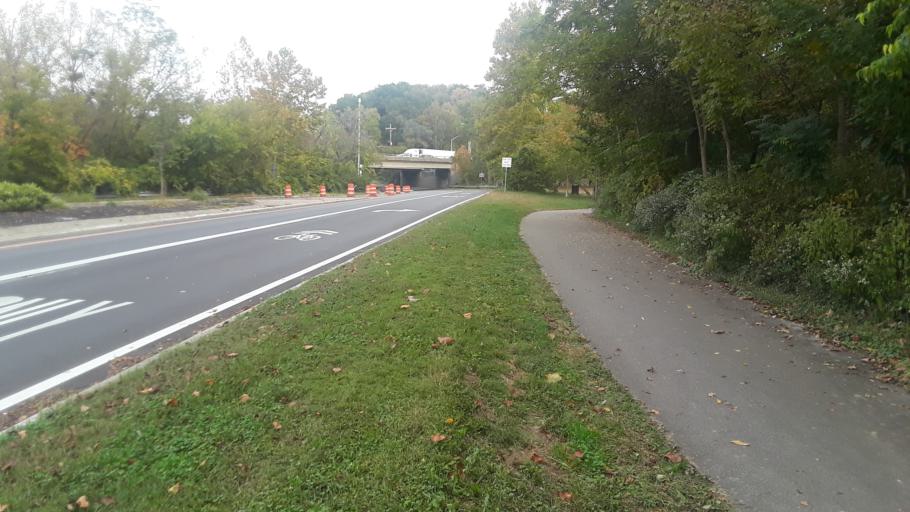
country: US
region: Kentucky
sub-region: Jefferson County
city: Saint Matthews
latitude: 38.2450
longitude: -85.6996
